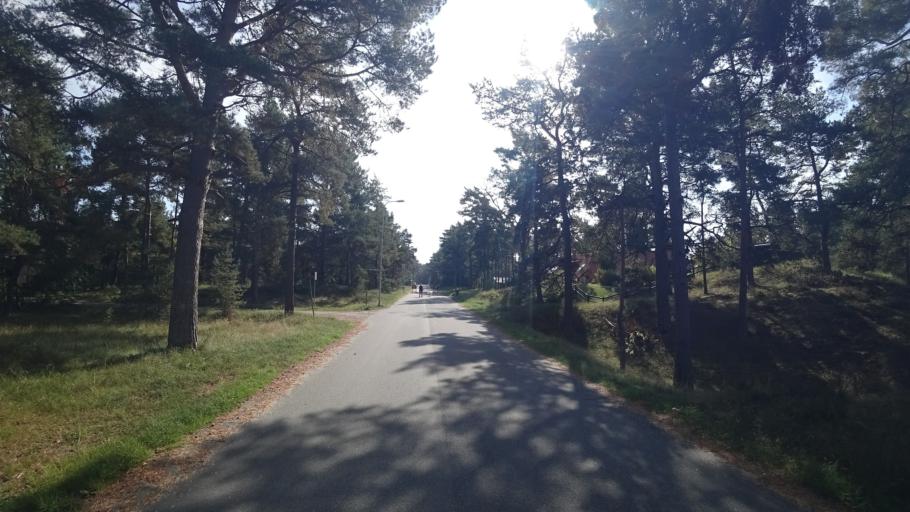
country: SE
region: Skane
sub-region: Kristianstads Kommun
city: Ahus
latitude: 55.9095
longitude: 14.2898
